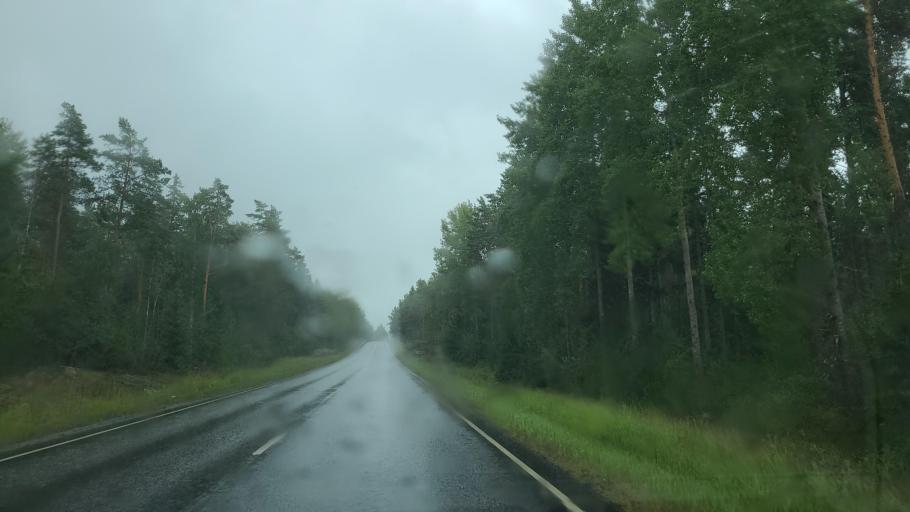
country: FI
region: Varsinais-Suomi
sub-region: Aboland-Turunmaa
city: Kimito
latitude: 60.2027
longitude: 22.6543
